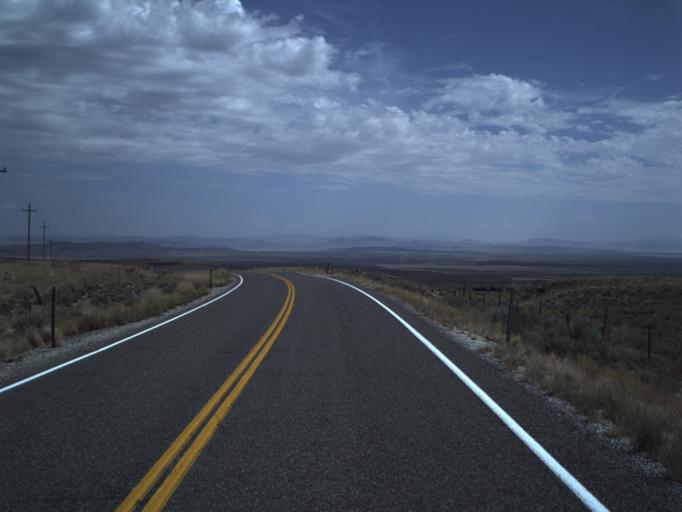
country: US
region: Idaho
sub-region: Cassia County
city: Burley
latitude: 41.8149
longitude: -113.2160
